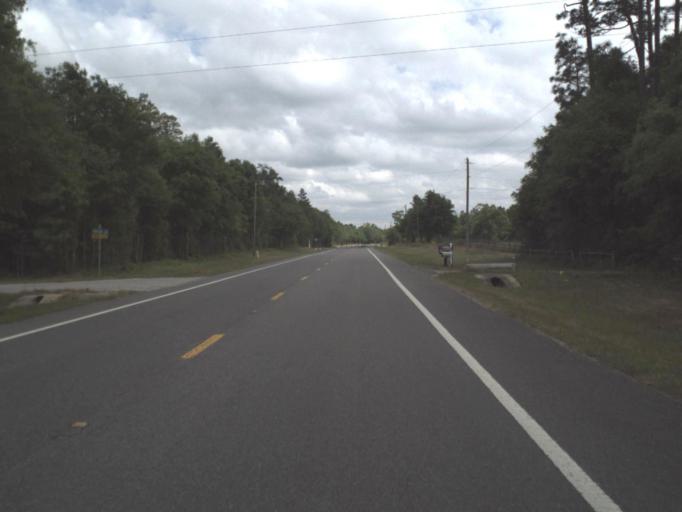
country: US
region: Florida
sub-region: Santa Rosa County
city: Point Baker
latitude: 30.7298
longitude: -87.0867
